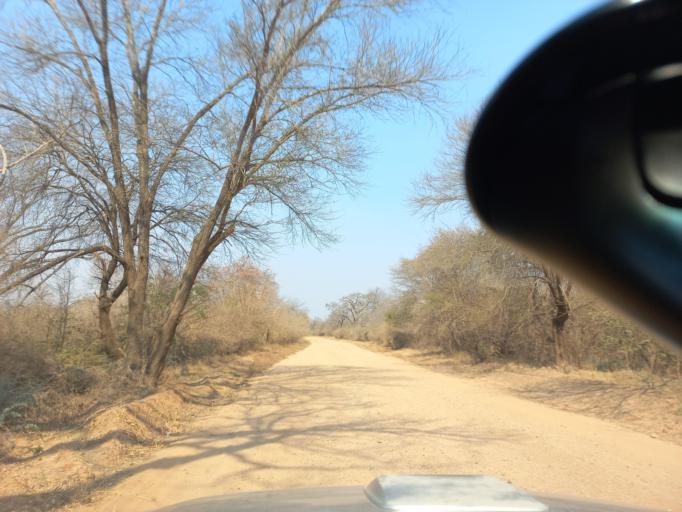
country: ZW
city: Chirundu
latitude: -15.9299
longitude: 28.9196
